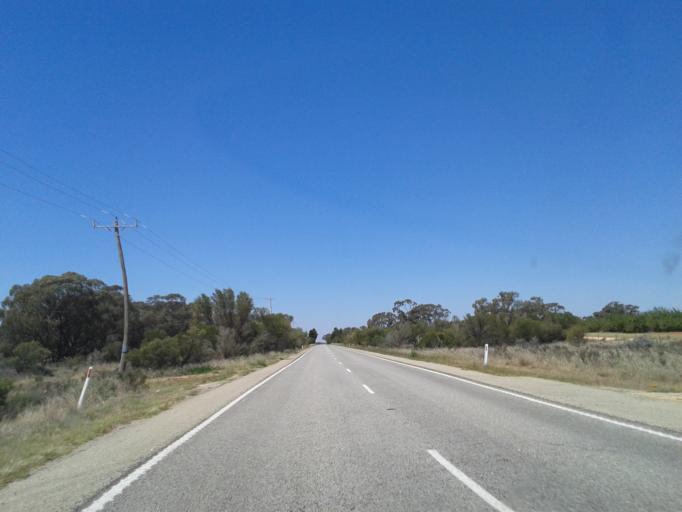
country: AU
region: Victoria
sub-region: Swan Hill
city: Swan Hill
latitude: -34.7063
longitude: 143.0471
